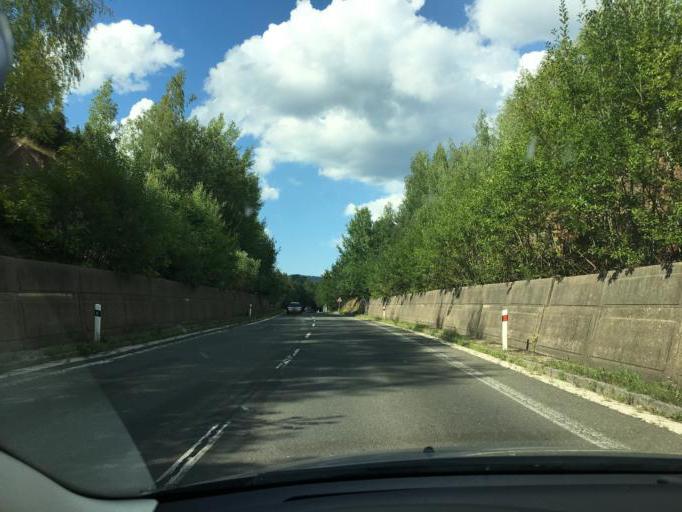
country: CZ
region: Kralovehradecky
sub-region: Okres Trutnov
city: Vrchlabi
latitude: 50.6249
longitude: 15.5971
